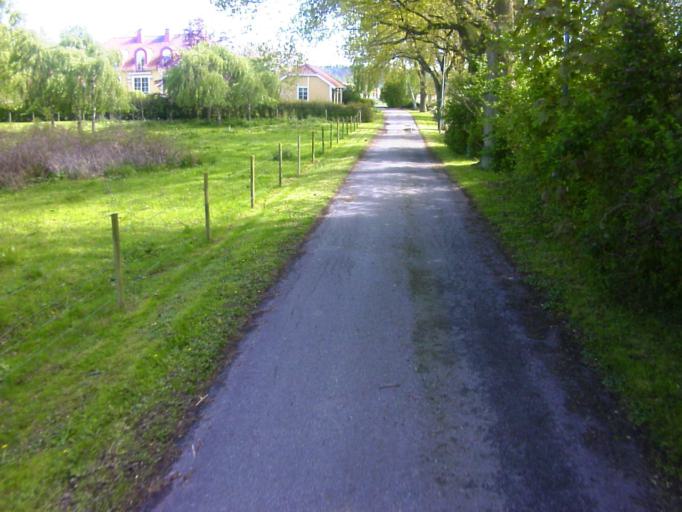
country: SE
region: Blekinge
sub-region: Solvesborgs Kommun
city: Soelvesborg
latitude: 56.0586
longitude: 14.6006
